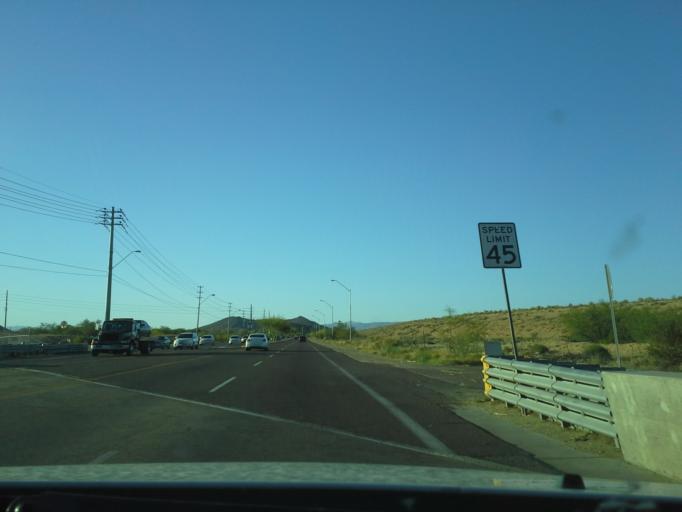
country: US
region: Arizona
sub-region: Maricopa County
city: Cave Creek
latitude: 33.6809
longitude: -112.0310
